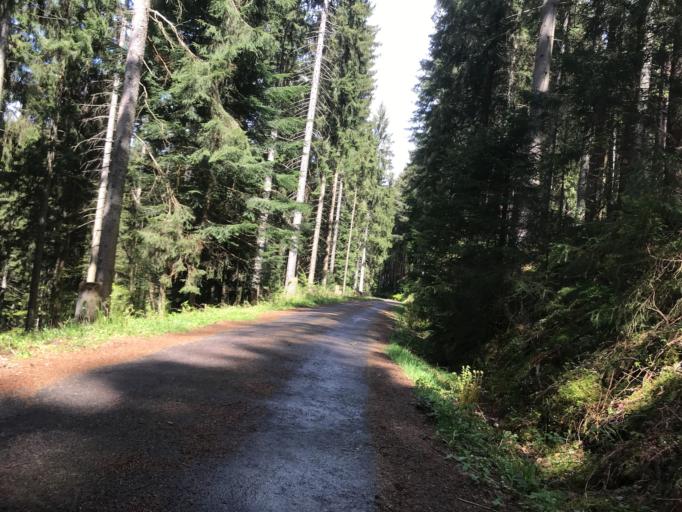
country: DE
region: Baden-Wuerttemberg
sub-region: Karlsruhe Region
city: Baiersbronn
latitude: 48.4804
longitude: 8.3375
